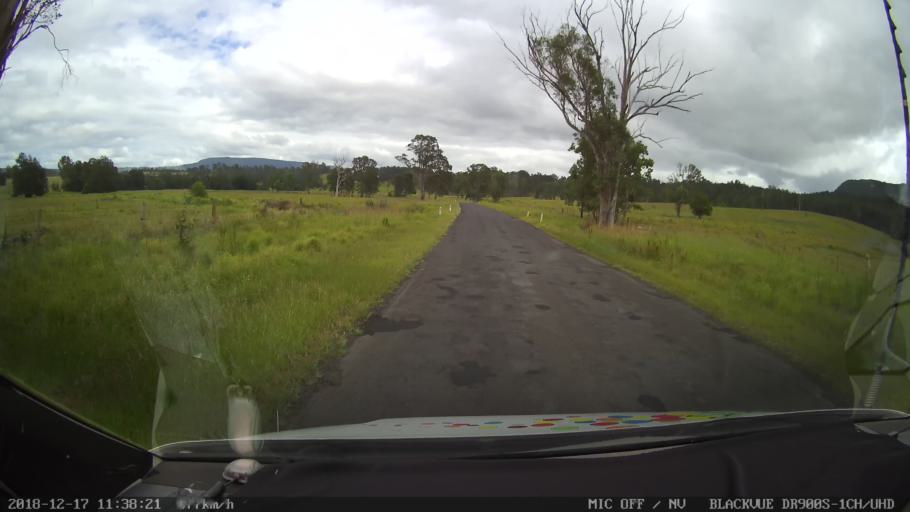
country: AU
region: New South Wales
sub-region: Kyogle
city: Kyogle
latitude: -28.6963
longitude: 152.6008
